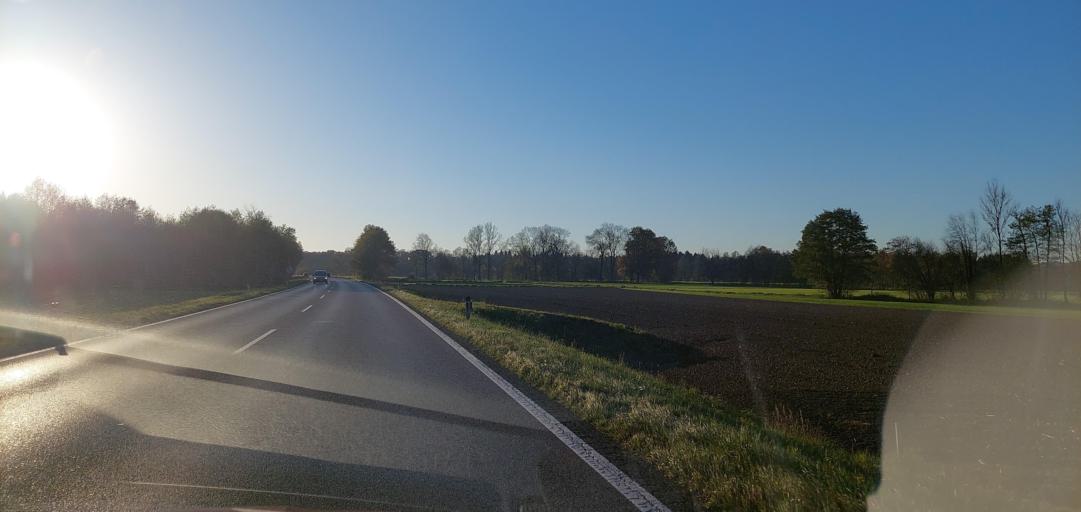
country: AT
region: Upper Austria
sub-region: Politischer Bezirk Grieskirchen
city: Grieskirchen
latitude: 48.2319
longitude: 13.7575
